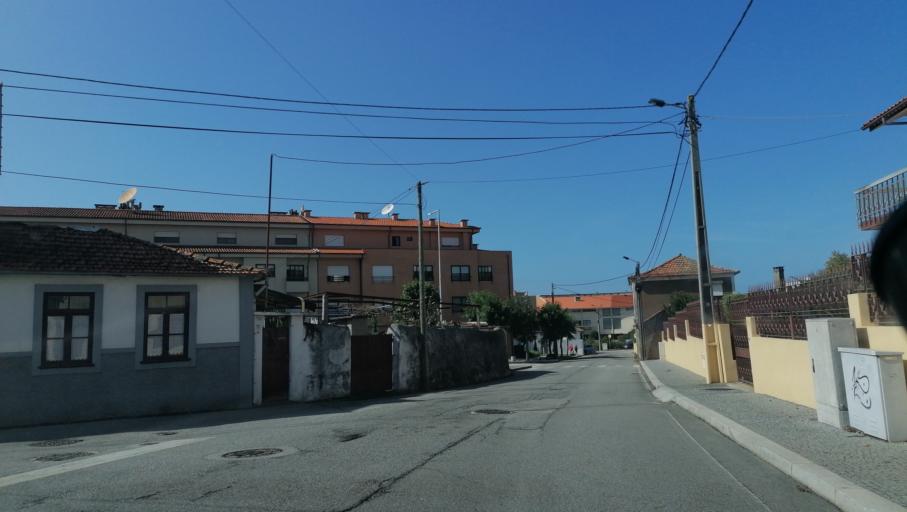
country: PT
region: Aveiro
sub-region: Espinho
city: Espinho
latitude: 41.0065
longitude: -8.6298
